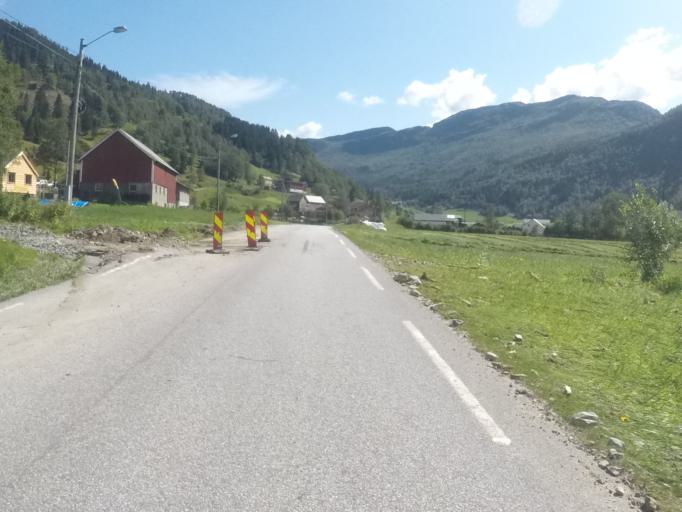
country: NO
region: Sogn og Fjordane
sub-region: Hoyanger
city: Hoyanger
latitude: 61.4209
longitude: 6.1535
